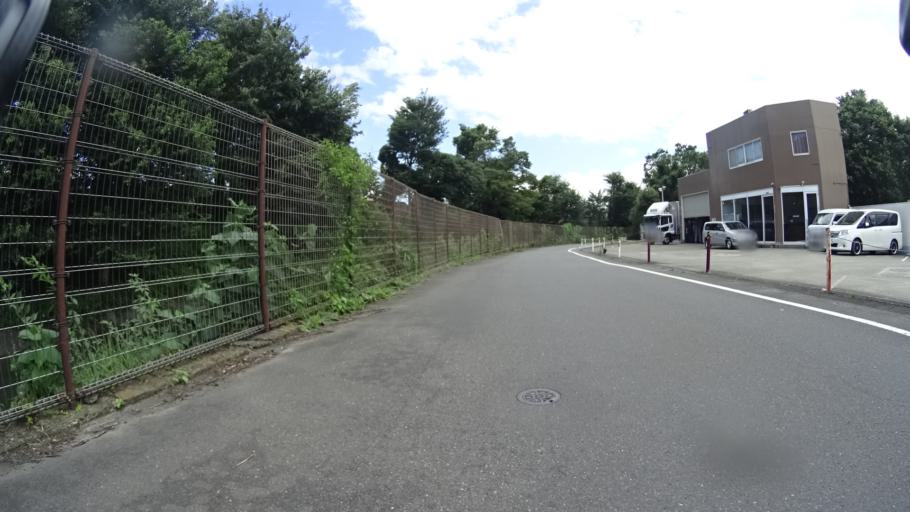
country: JP
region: Tokyo
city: Fussa
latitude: 35.7376
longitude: 139.3257
